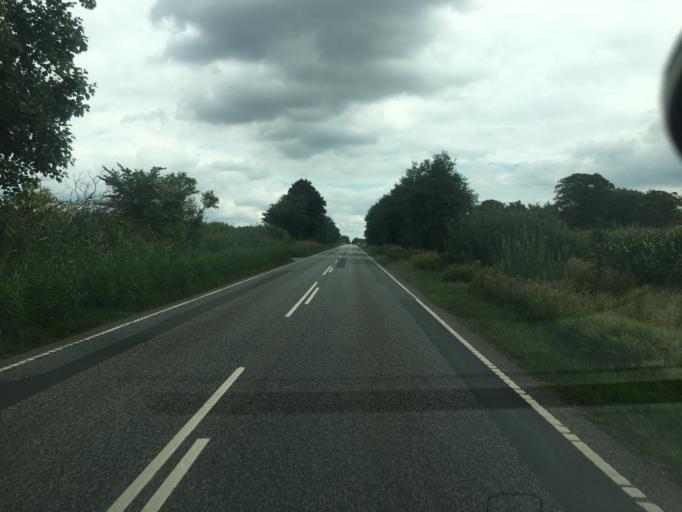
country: DK
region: South Denmark
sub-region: Tonder Kommune
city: Toftlund
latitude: 55.1224
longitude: 9.0795
